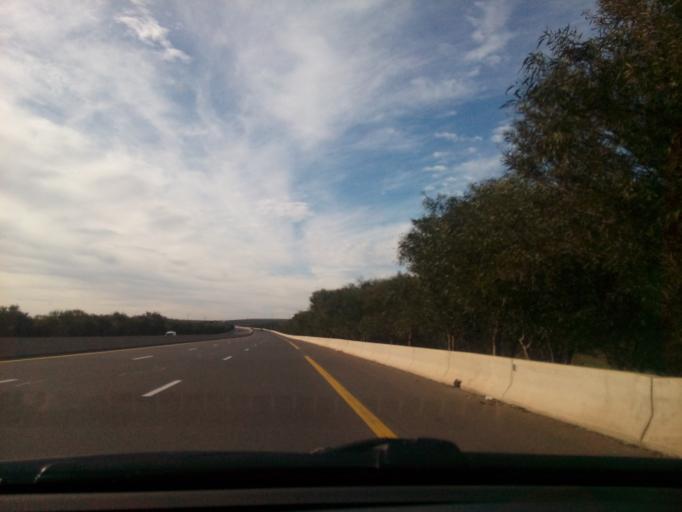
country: DZ
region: Sidi Bel Abbes
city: Sidi Bel Abbes
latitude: 35.1642
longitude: -0.7702
